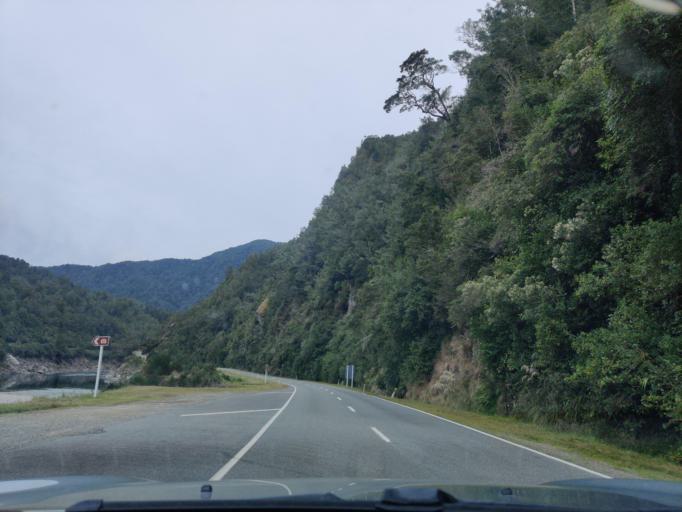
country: NZ
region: West Coast
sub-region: Buller District
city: Westport
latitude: -41.8494
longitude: 171.7351
